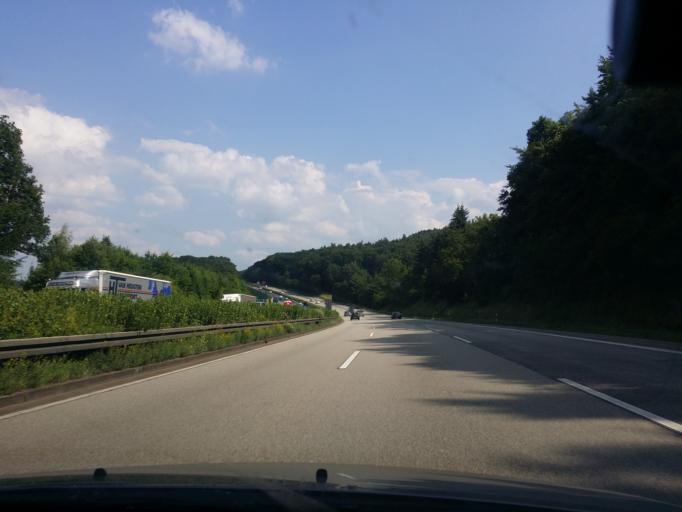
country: DE
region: Hesse
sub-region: Regierungsbezirk Darmstadt
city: Idstein
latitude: 50.1790
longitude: 8.2707
